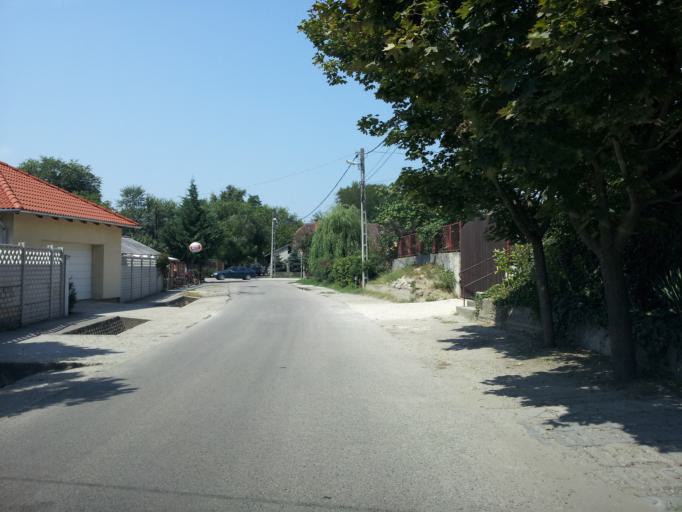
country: HU
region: Pest
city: Szigetszentmiklos
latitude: 47.3366
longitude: 19.0367
